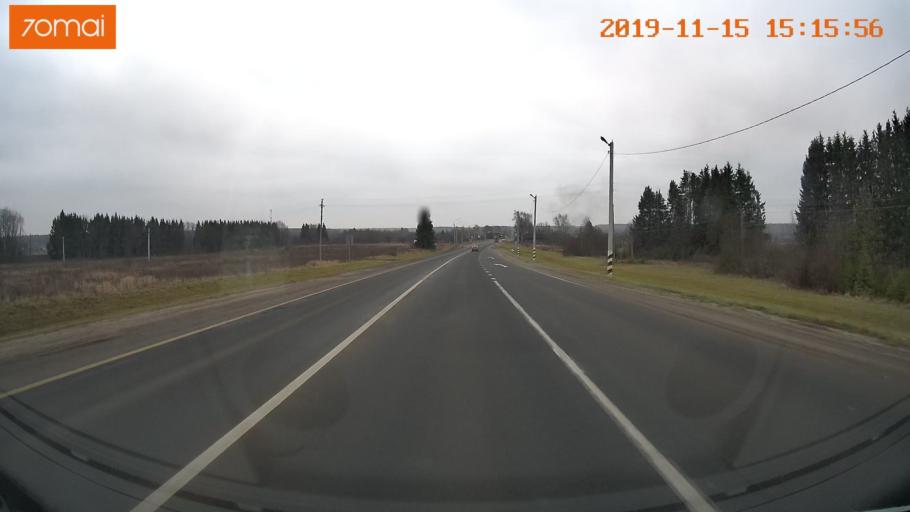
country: RU
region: Jaroslavl
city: Danilov
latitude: 58.2780
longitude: 40.1958
